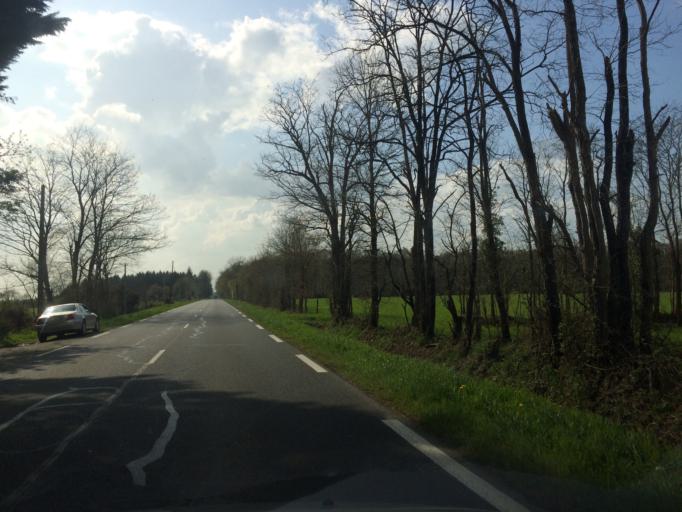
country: FR
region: Pays de la Loire
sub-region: Departement de la Loire-Atlantique
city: Blain
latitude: 47.4852
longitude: -1.8290
